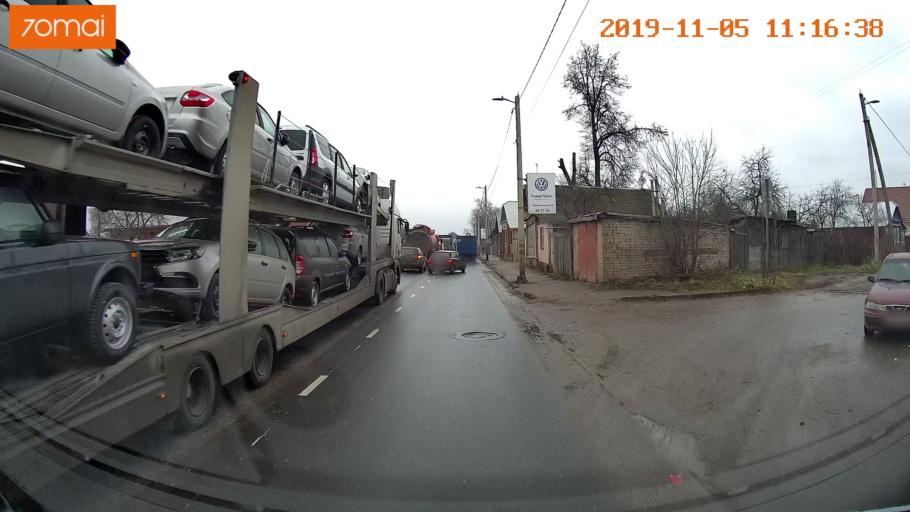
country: RU
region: Ivanovo
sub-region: Gorod Ivanovo
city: Ivanovo
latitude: 56.9864
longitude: 40.9533
